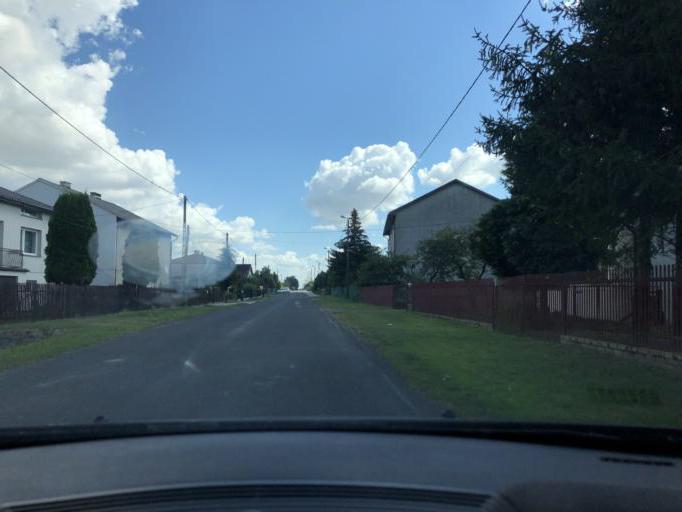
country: PL
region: Lodz Voivodeship
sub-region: Powiat wieruszowski
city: Walichnowy
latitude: 51.2614
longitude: 18.3840
